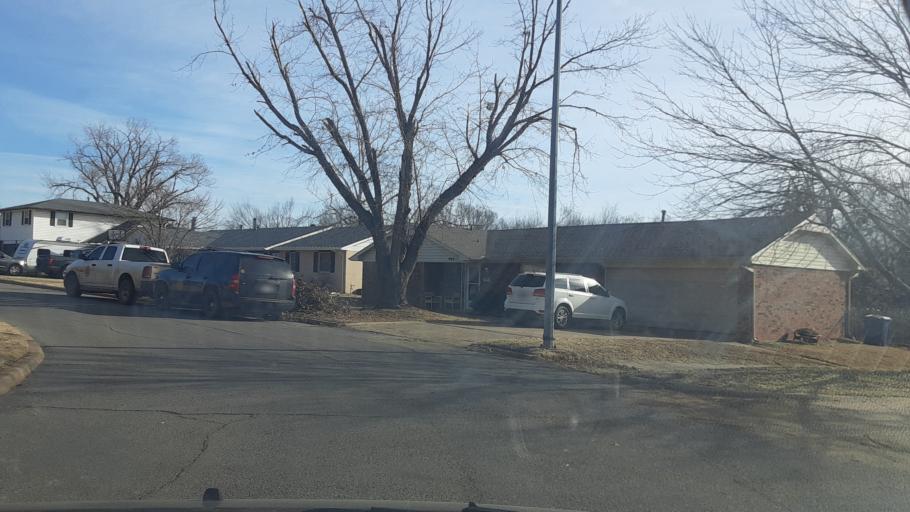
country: US
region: Oklahoma
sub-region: Logan County
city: Guthrie
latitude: 35.8911
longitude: -97.4150
